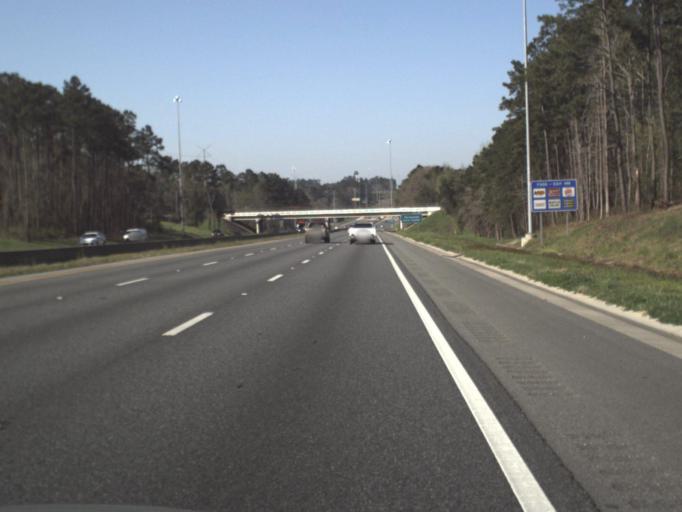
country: US
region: Florida
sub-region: Leon County
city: Tallahassee
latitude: 30.4880
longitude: -84.2918
